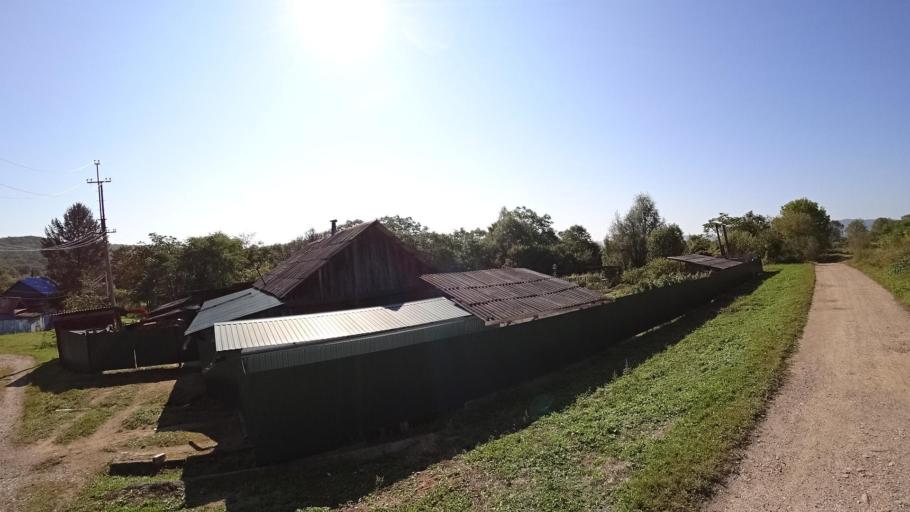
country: RU
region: Jewish Autonomous Oblast
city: Bira
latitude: 49.0063
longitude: 132.4745
